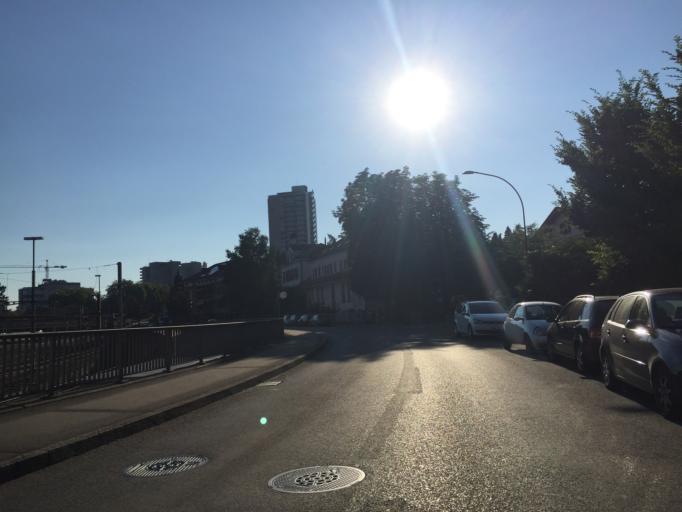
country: CH
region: Bern
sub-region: Bern-Mittelland District
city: Bern
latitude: 46.9490
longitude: 7.4339
